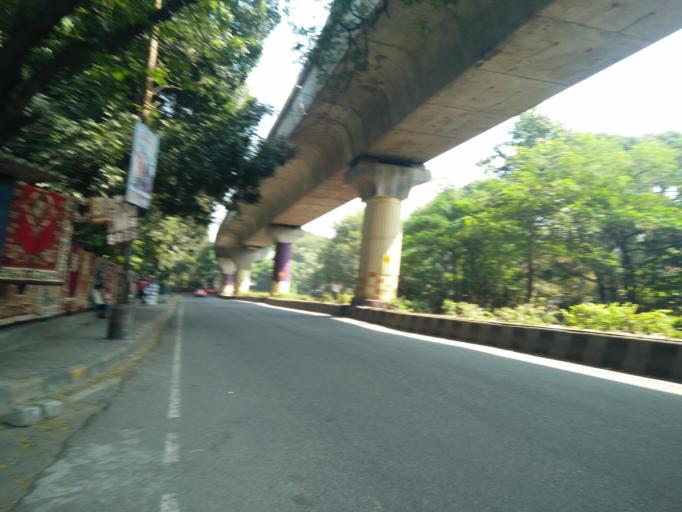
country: IN
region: Karnataka
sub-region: Bangalore Urban
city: Bangalore
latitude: 12.9740
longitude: 77.5423
